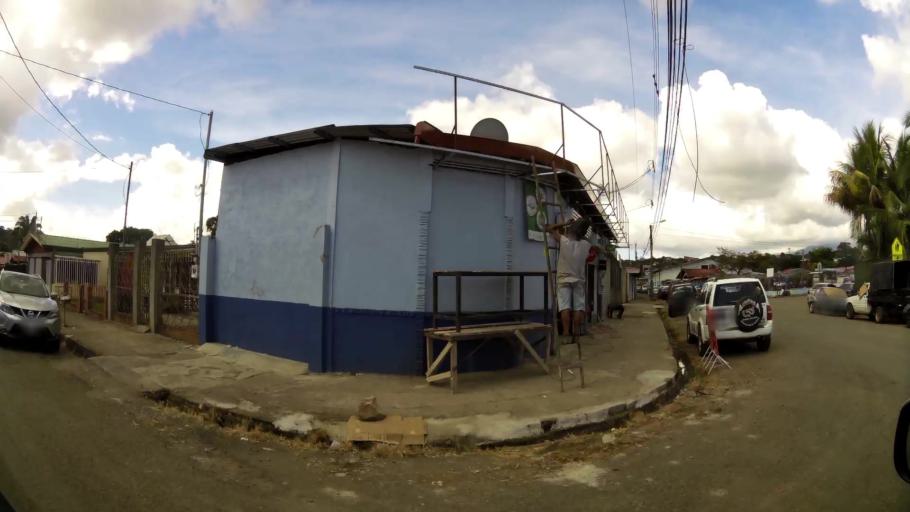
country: CR
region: San Jose
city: San Isidro
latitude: 9.3664
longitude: -83.7041
